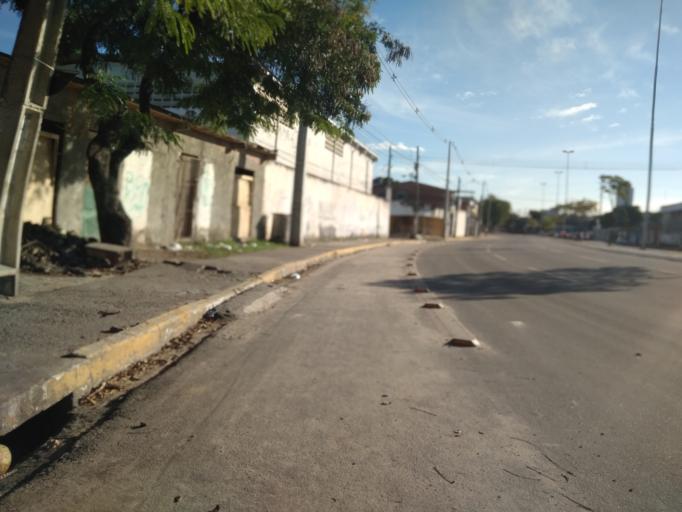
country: BR
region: Pernambuco
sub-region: Recife
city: Recife
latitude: -8.0792
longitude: -34.9322
